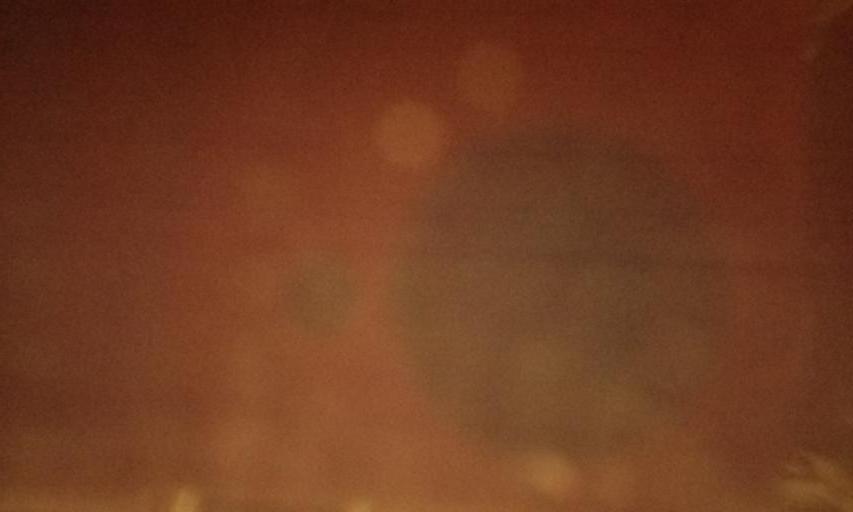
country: JP
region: Okayama
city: Okayama-shi
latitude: 34.7232
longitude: 134.0937
